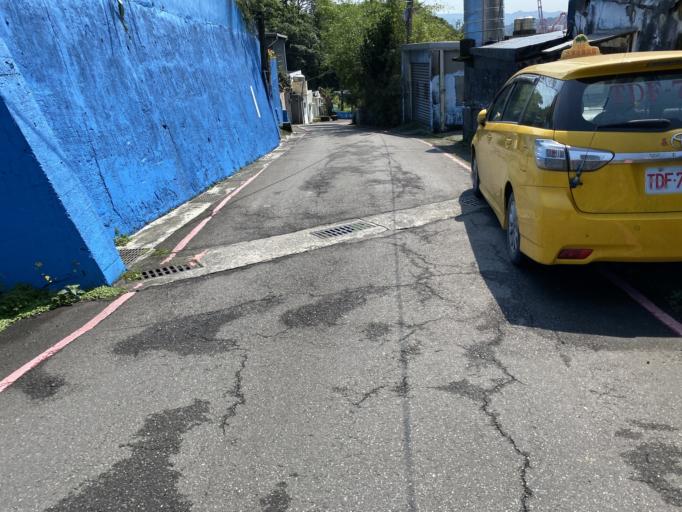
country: TW
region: Taiwan
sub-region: Keelung
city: Keelung
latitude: 25.1547
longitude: 121.7439
